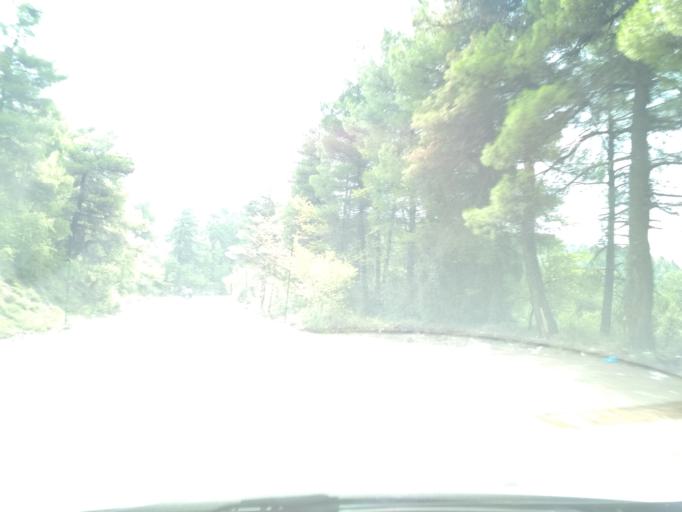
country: GR
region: Central Greece
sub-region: Nomos Evvoias
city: Politika
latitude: 38.6662
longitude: 23.5562
